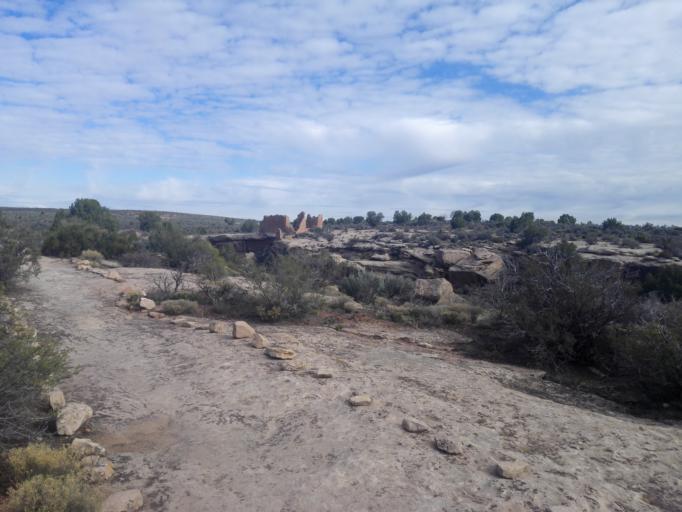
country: US
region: Colorado
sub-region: Montezuma County
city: Towaoc
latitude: 37.3844
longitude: -109.0802
